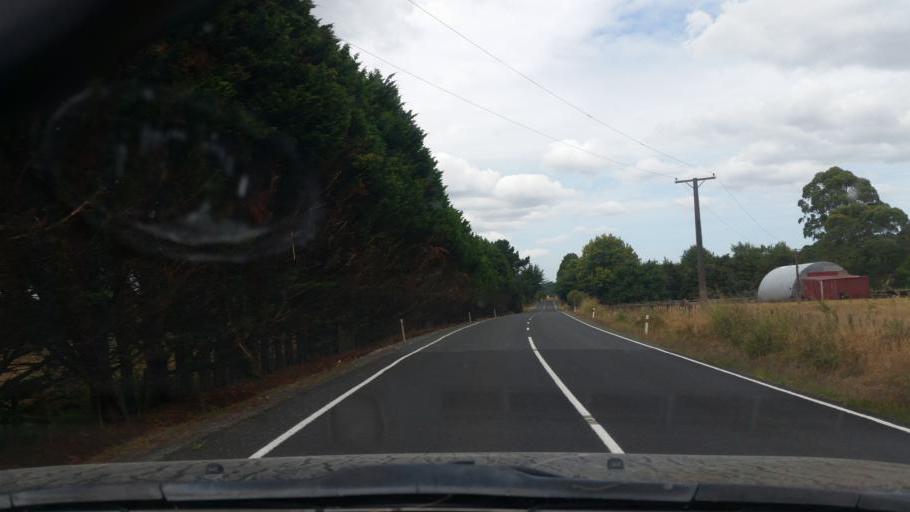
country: NZ
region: Northland
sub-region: Kaipara District
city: Dargaville
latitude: -35.7898
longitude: 173.7253
